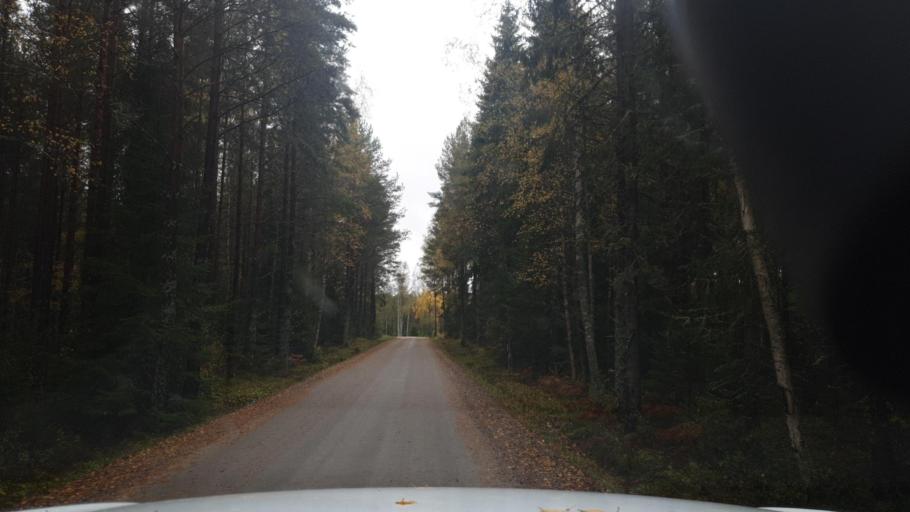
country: SE
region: Vaermland
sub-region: Karlstads Kommun
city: Edsvalla
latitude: 59.5256
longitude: 13.0011
